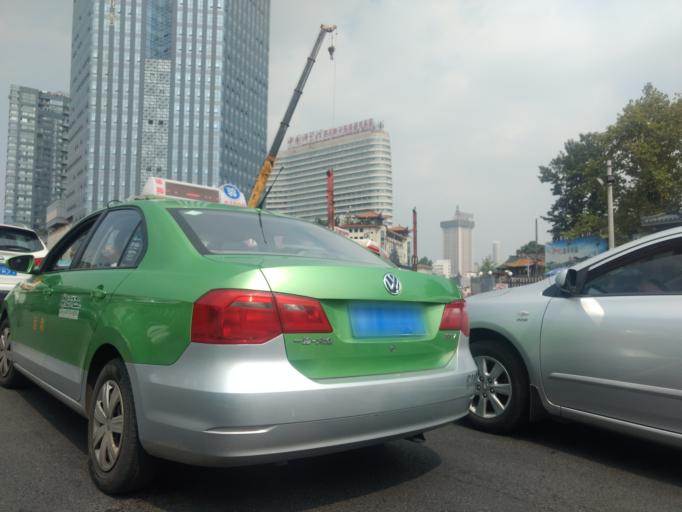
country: CN
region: Sichuan
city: Chengdu
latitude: 30.6614
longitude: 104.0386
